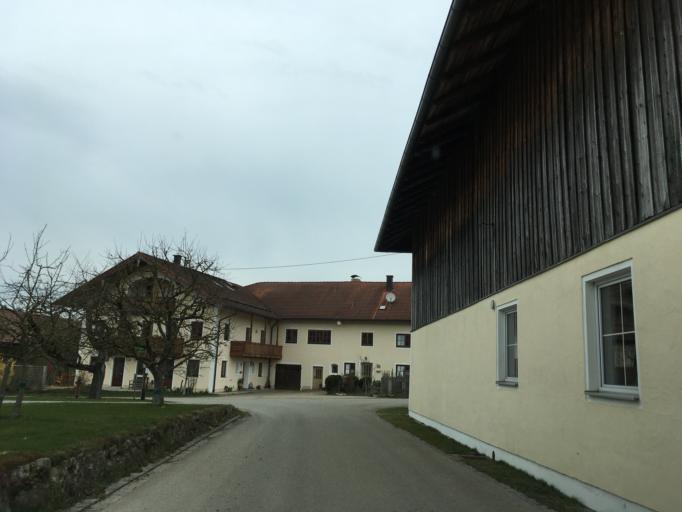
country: DE
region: Bavaria
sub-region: Upper Bavaria
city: Schnaitsee
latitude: 48.0538
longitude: 12.3730
